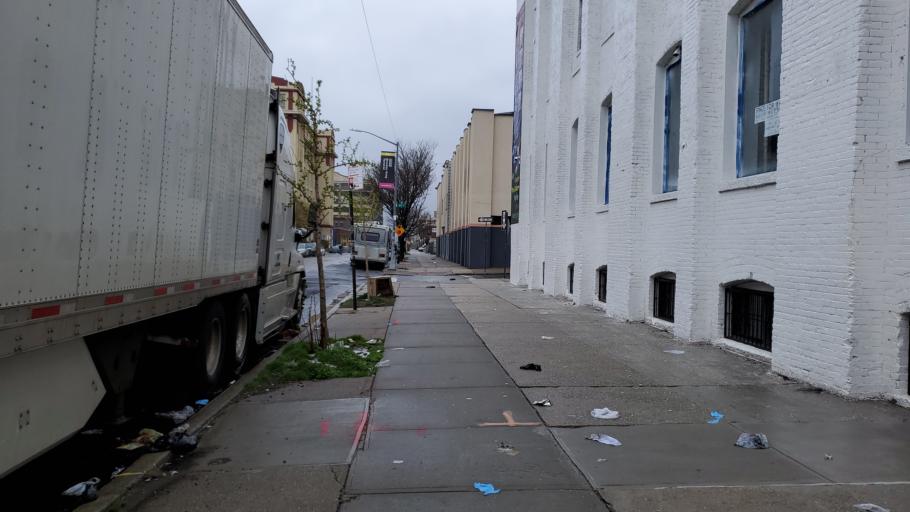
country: US
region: New York
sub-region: Kings County
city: Bensonhurst
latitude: 40.6516
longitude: -74.0142
